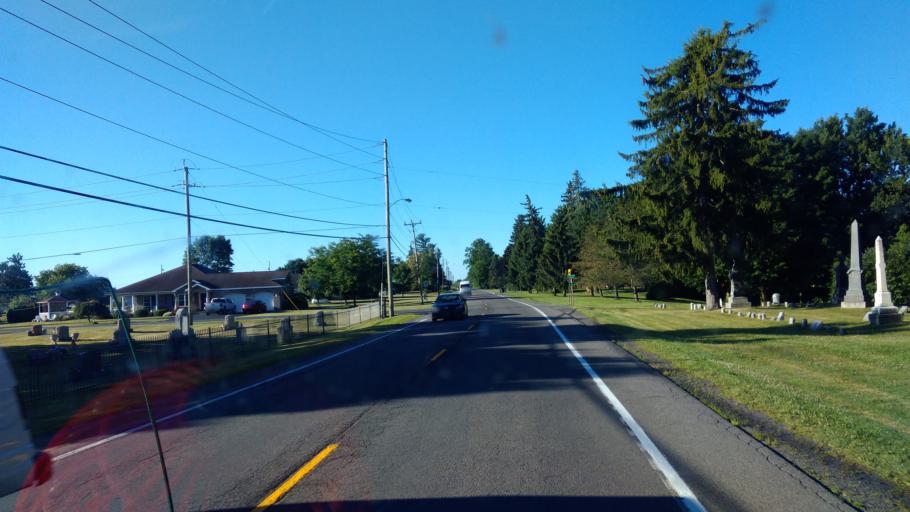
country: US
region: New York
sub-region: Wayne County
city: Lyons
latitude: 43.0466
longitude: -76.9939
